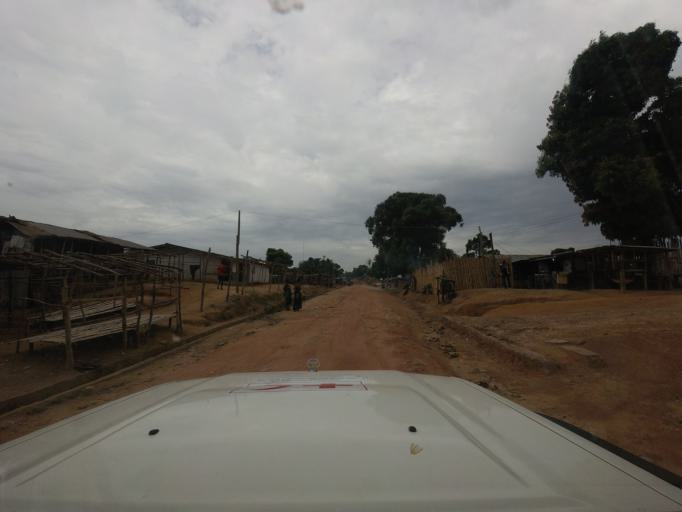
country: SL
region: Eastern Province
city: Buedu
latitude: 8.2830
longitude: -10.0880
